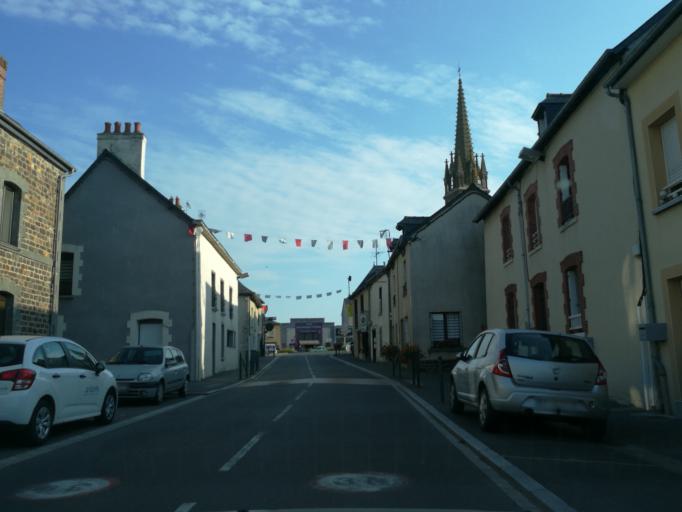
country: FR
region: Brittany
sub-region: Departement d'Ille-et-Vilaine
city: Bedee
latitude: 48.1791
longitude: -1.9449
